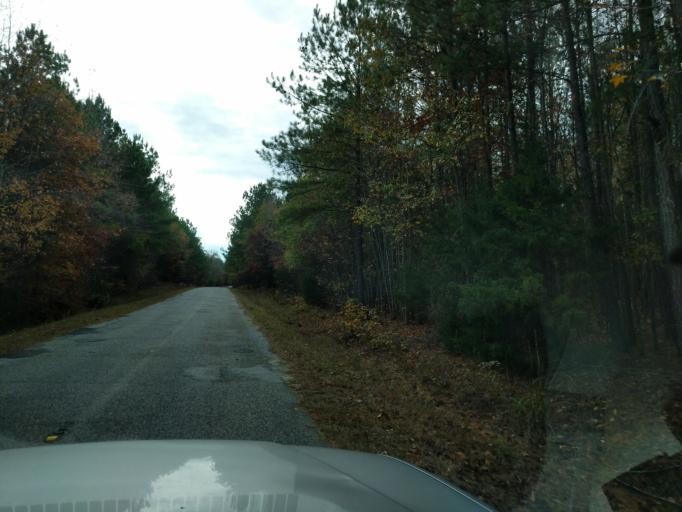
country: US
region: South Carolina
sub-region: Laurens County
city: Watts Mills
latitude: 34.5409
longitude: -81.9408
